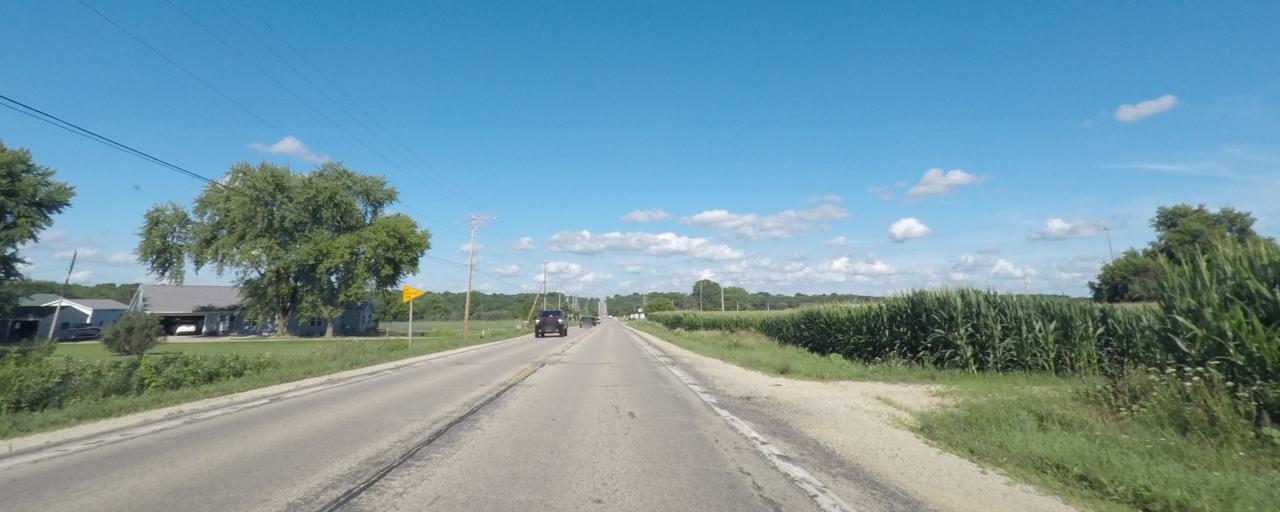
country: US
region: Wisconsin
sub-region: Rock County
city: Janesville
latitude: 42.7302
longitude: -89.0708
